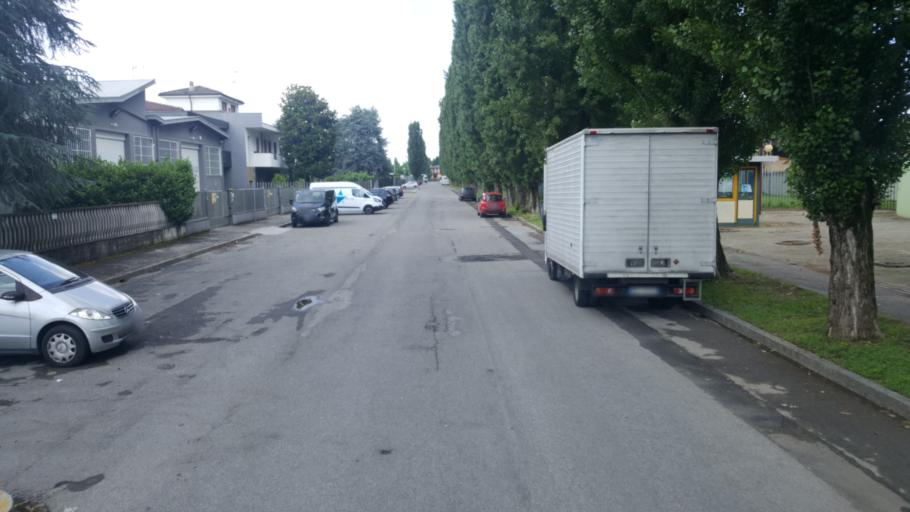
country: IT
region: Lombardy
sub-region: Citta metropolitana di Milano
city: Melzo
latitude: 45.4930
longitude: 9.4182
